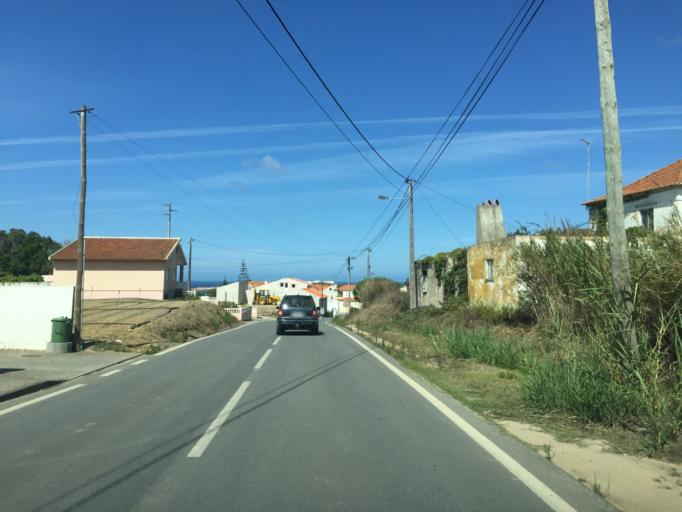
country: PT
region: Lisbon
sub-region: Lourinha
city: Lourinha
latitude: 39.2699
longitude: -9.3048
